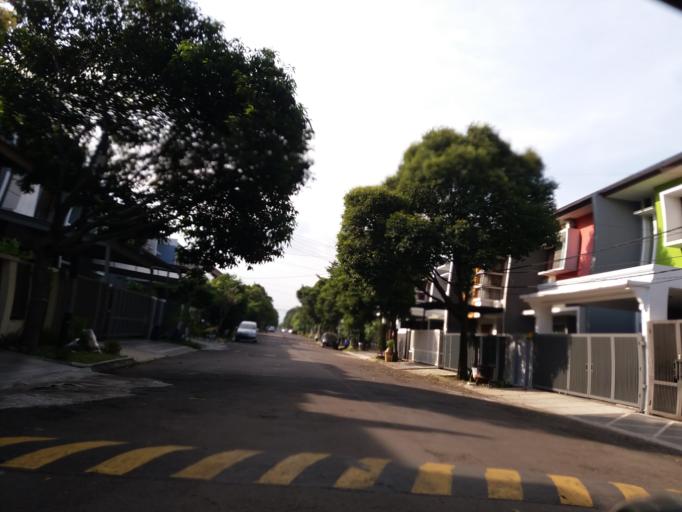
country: ID
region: West Java
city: Bandung
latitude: -6.9628
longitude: 107.6299
